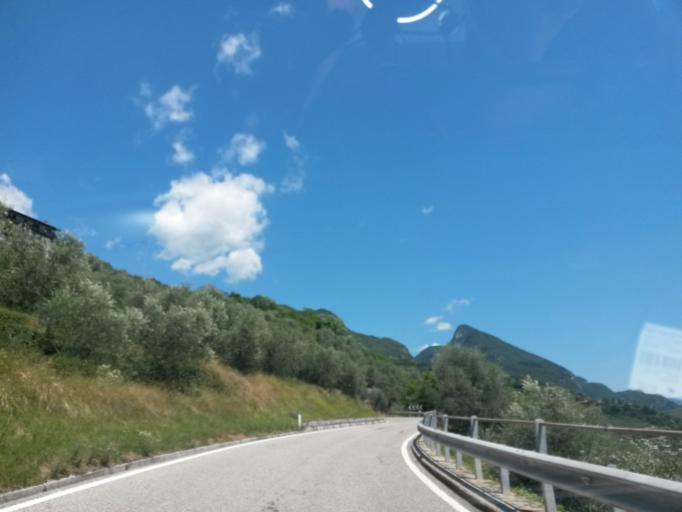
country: IT
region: Trentino-Alto Adige
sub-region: Provincia di Trento
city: Tenno
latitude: 45.9038
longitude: 10.8336
